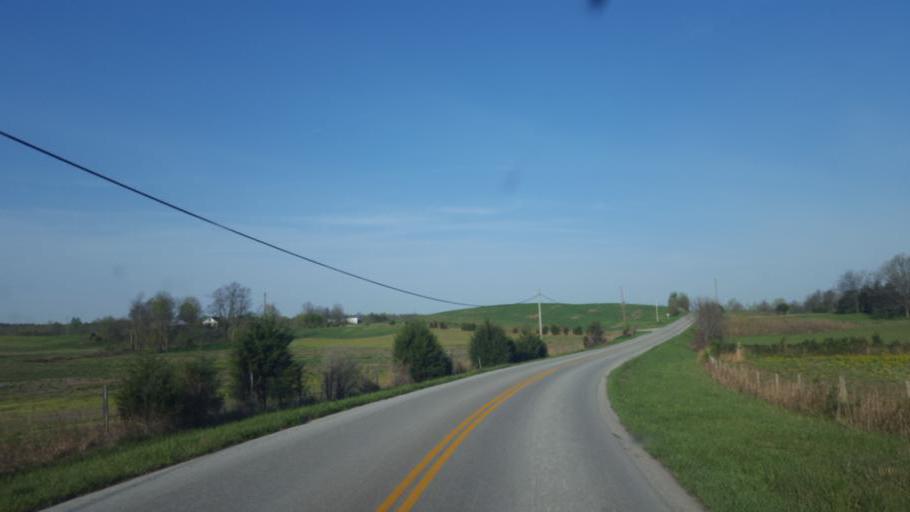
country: US
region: Kentucky
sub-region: Hardin County
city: Elizabethtown
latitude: 37.4951
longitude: -85.9521
